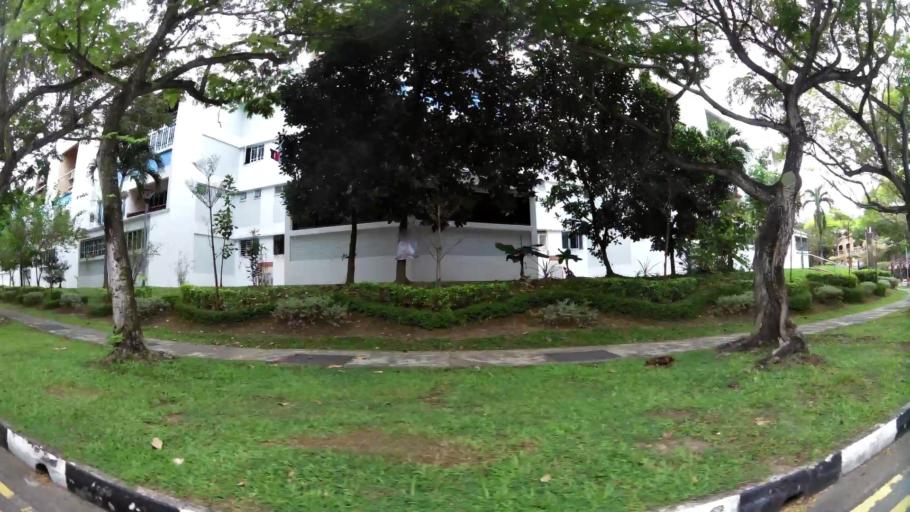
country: SG
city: Singapore
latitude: 1.3690
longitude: 103.8737
